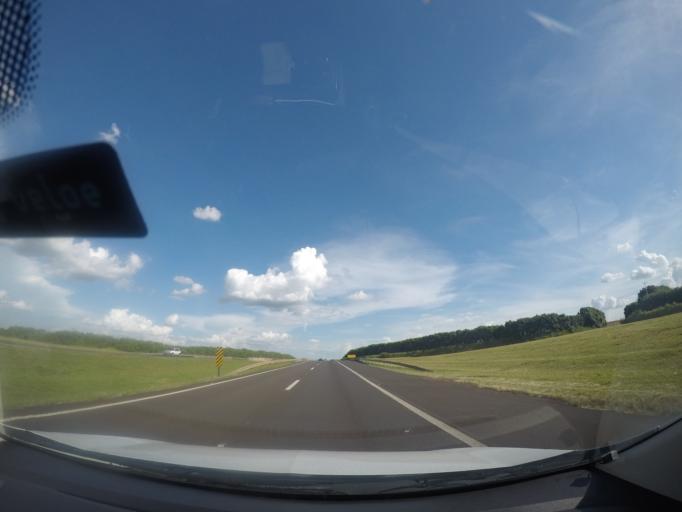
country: BR
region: Sao Paulo
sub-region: Bebedouro
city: Bebedouro
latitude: -21.0077
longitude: -48.4283
